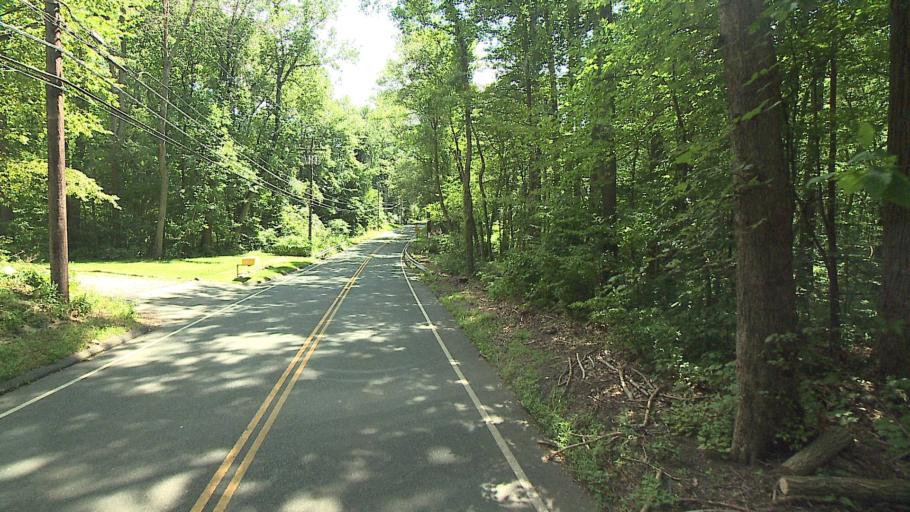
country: US
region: Connecticut
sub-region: Fairfield County
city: Trumbull
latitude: 41.2589
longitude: -73.1655
